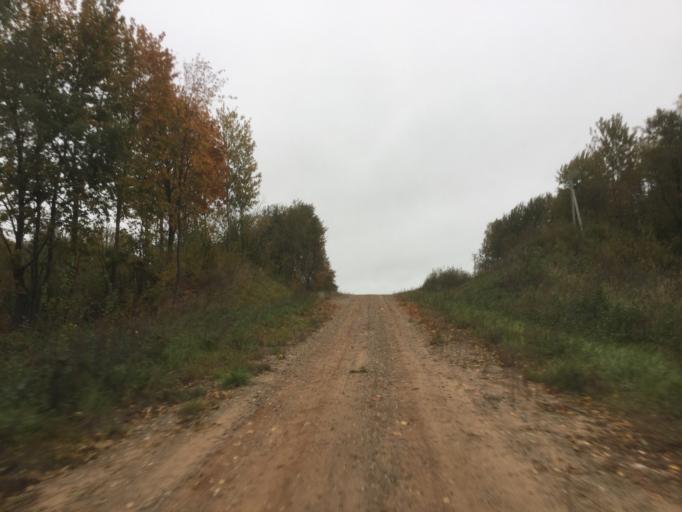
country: BY
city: Novolukoml'
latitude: 54.7335
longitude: 29.1378
